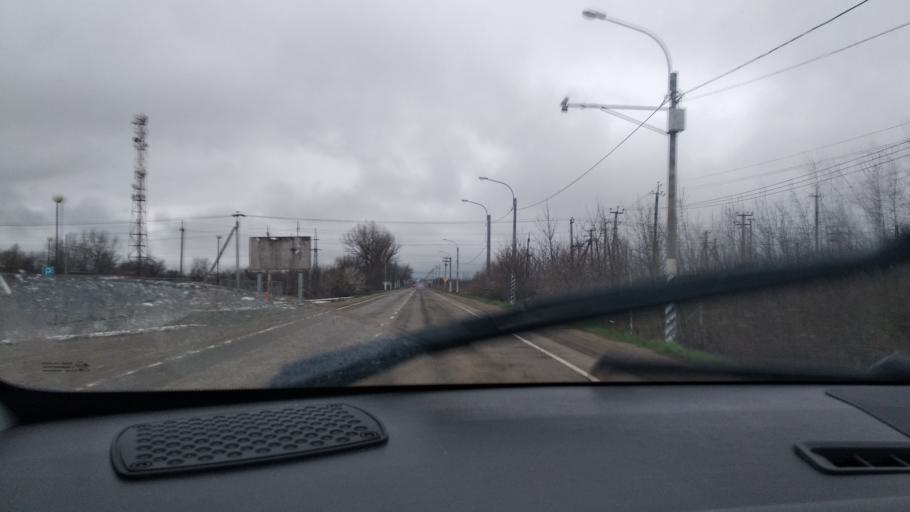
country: RU
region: Krasnodarskiy
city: Afipskiy
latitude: 44.8953
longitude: 38.8256
